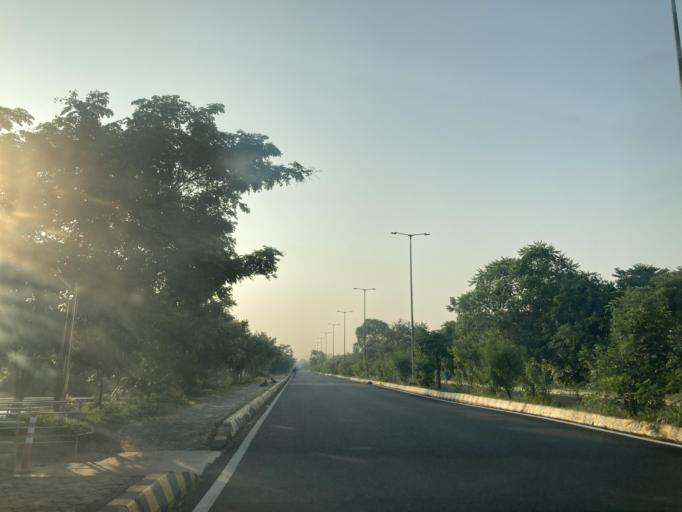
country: IN
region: Odisha
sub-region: Khordha
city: Bhubaneshwar
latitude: 20.2531
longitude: 85.8203
